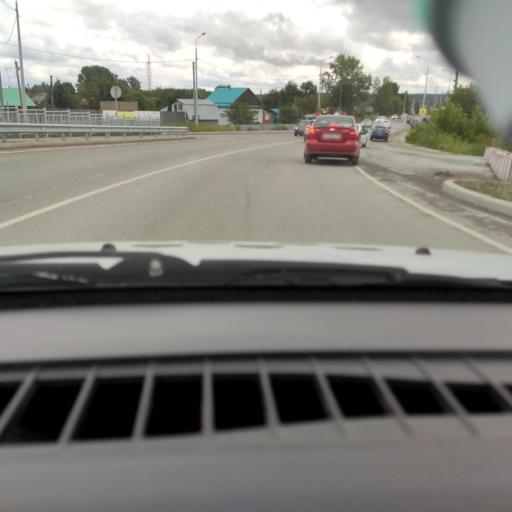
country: RU
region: Sverdlovsk
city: Krasnoufimsk
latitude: 56.6136
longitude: 57.7862
